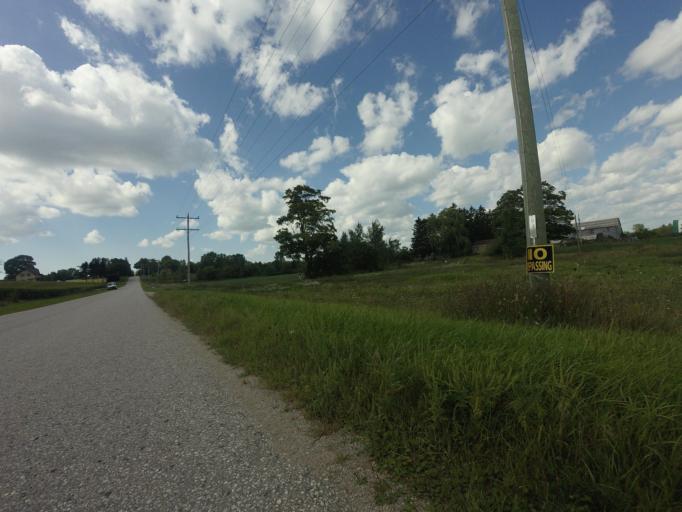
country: CA
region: Ontario
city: Huron East
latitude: 43.7302
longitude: -81.4144
